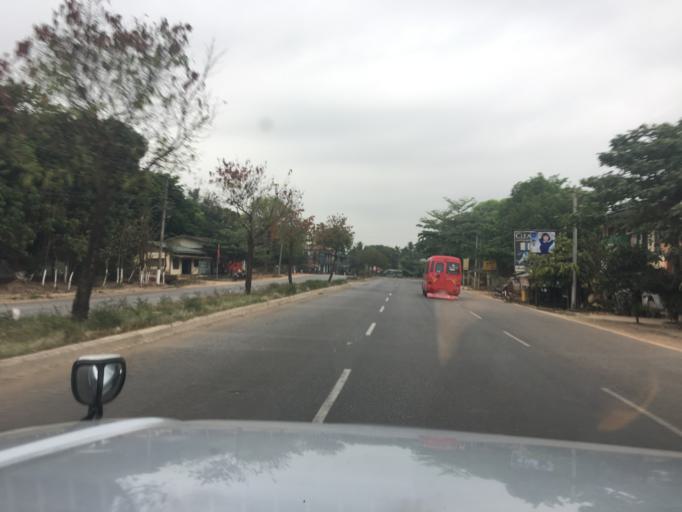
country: MM
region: Bago
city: Thanatpin
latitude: 17.1830
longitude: 96.3811
